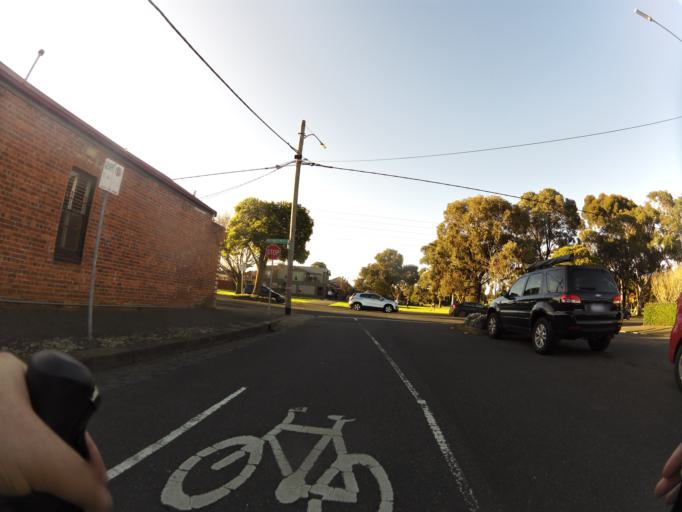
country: AU
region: Victoria
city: Carlton North
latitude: -37.7803
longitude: 144.9643
